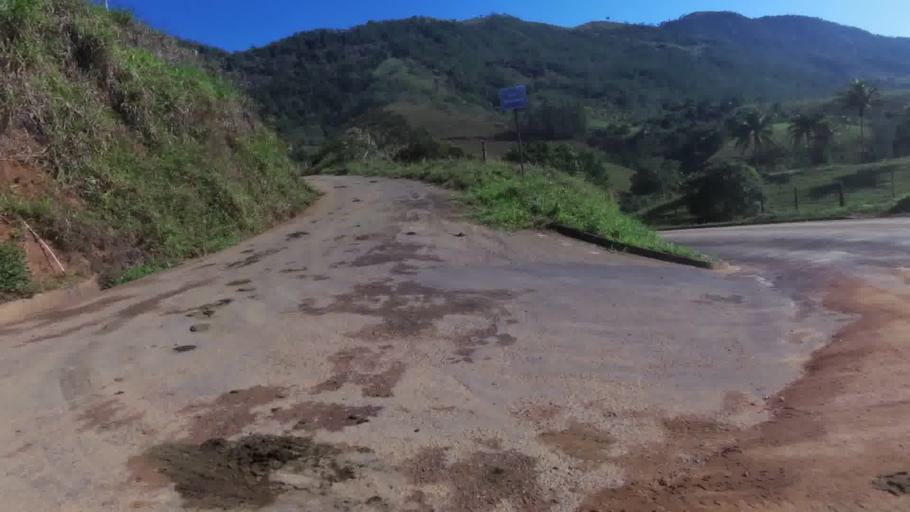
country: BR
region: Espirito Santo
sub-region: Alfredo Chaves
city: Alfredo Chaves
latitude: -20.6816
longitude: -40.7731
